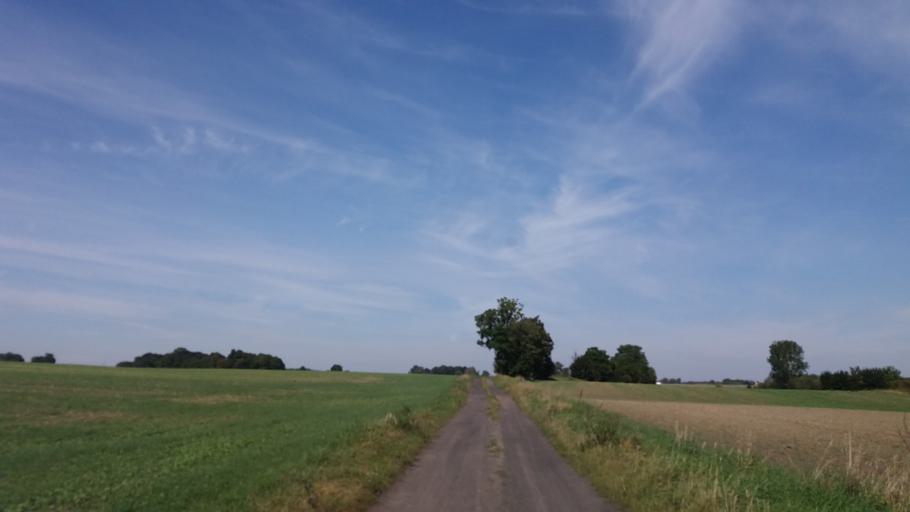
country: PL
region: West Pomeranian Voivodeship
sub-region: Powiat choszczenski
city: Choszczno
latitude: 53.1317
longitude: 15.4053
